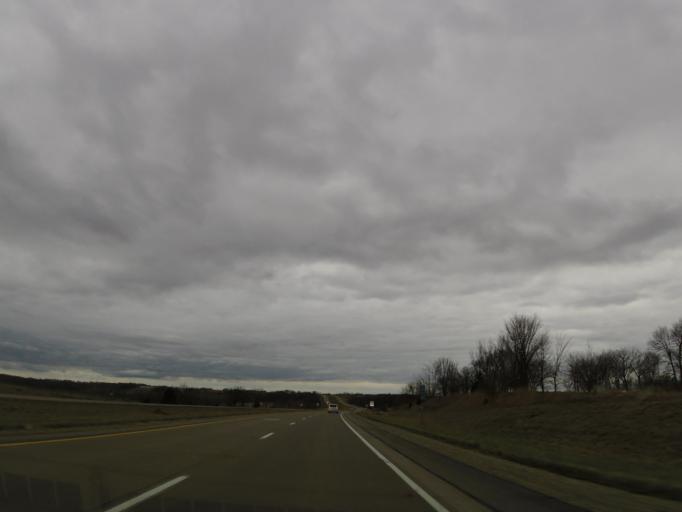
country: US
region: Iowa
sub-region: Henry County
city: Winfield
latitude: 41.1874
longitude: -91.5310
